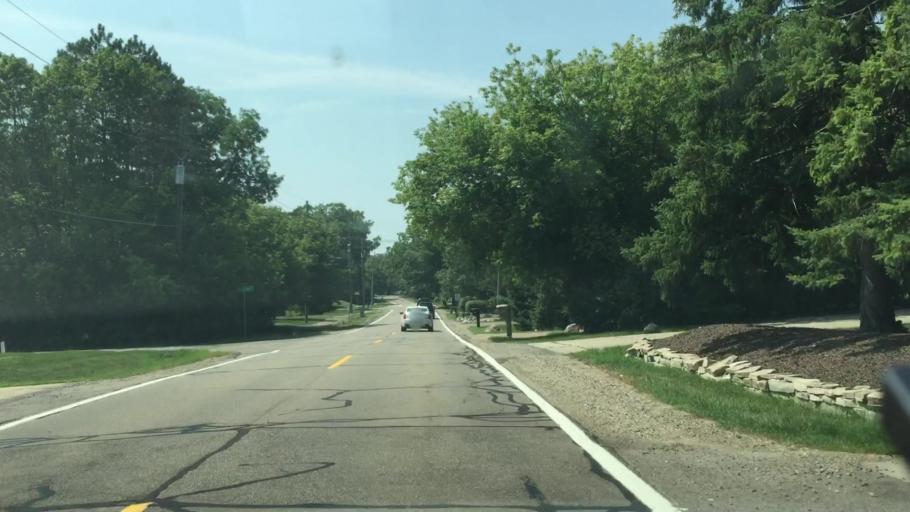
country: US
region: Michigan
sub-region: Oakland County
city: Franklin
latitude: 42.5535
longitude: -83.3290
